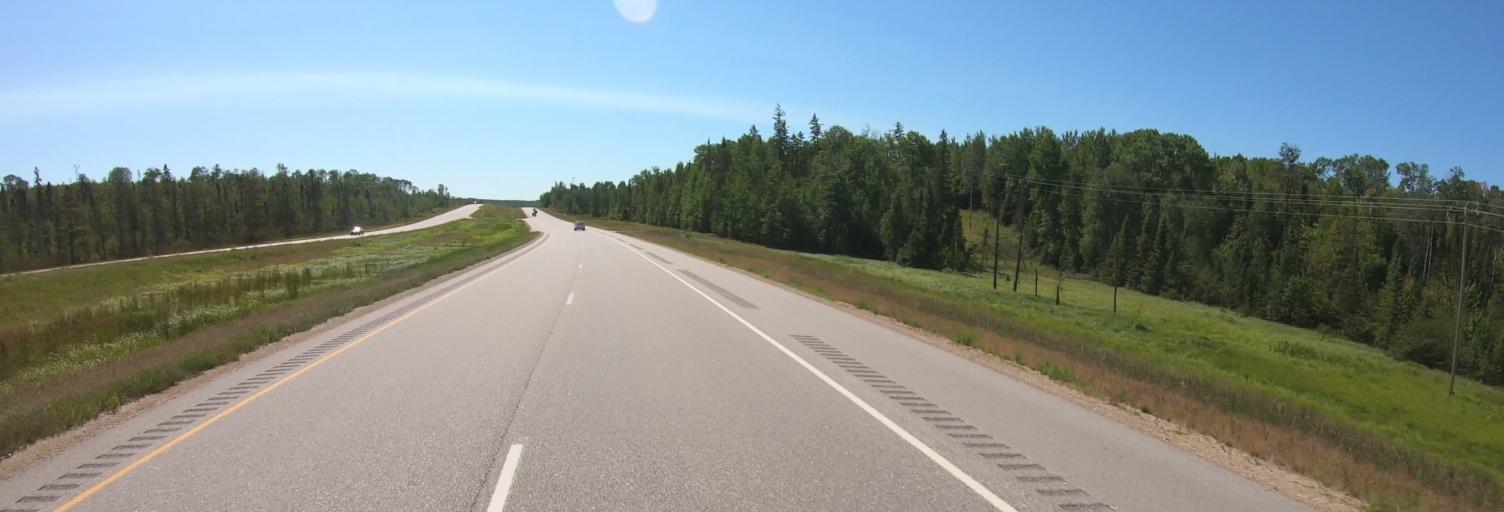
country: US
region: Minnesota
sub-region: Saint Louis County
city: Mountain Iron
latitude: 47.7557
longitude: -92.6528
